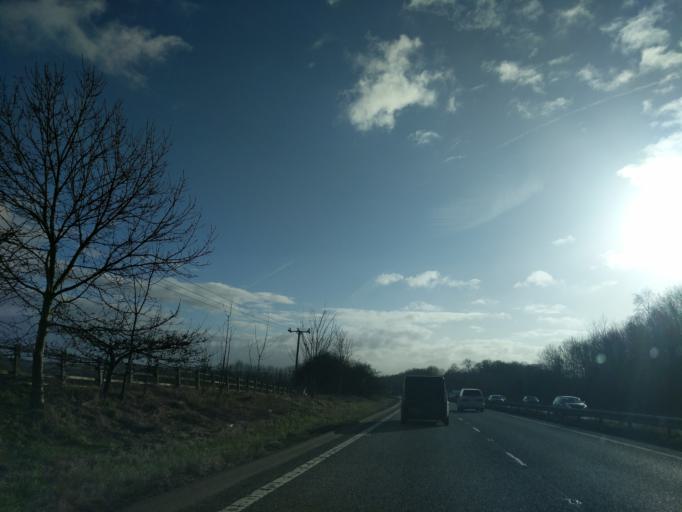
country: GB
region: England
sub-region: Derbyshire
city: Kilburn
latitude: 53.0273
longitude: -1.4427
